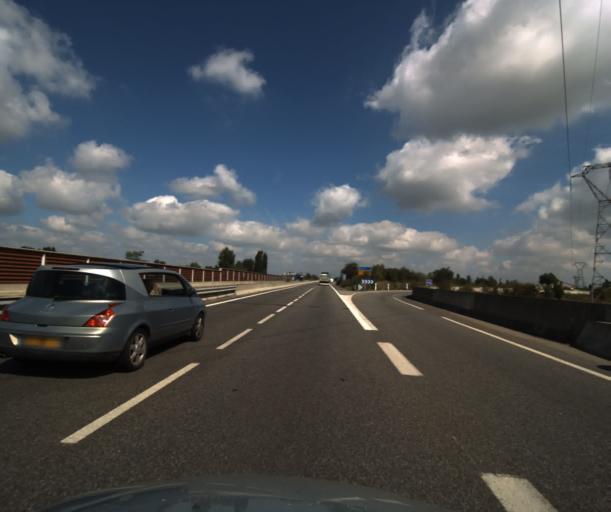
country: FR
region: Midi-Pyrenees
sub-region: Departement de la Haute-Garonne
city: Pinsaguel
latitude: 43.5137
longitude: 1.3804
